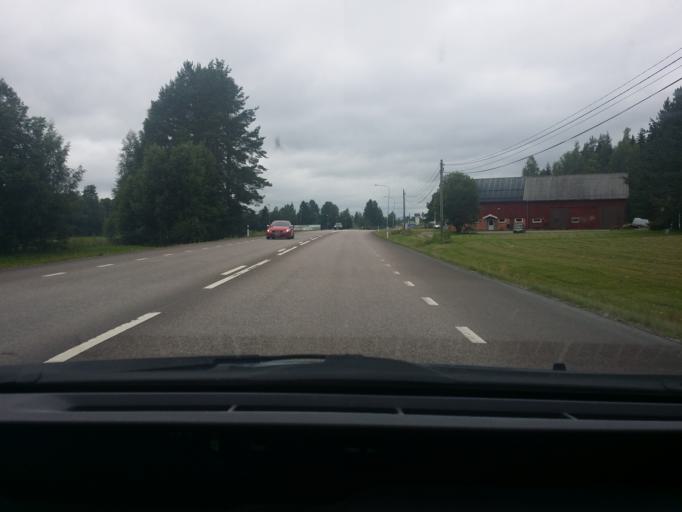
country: SE
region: Dalarna
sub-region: Gagnefs Kommun
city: Djuras
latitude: 60.5566
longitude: 15.1443
